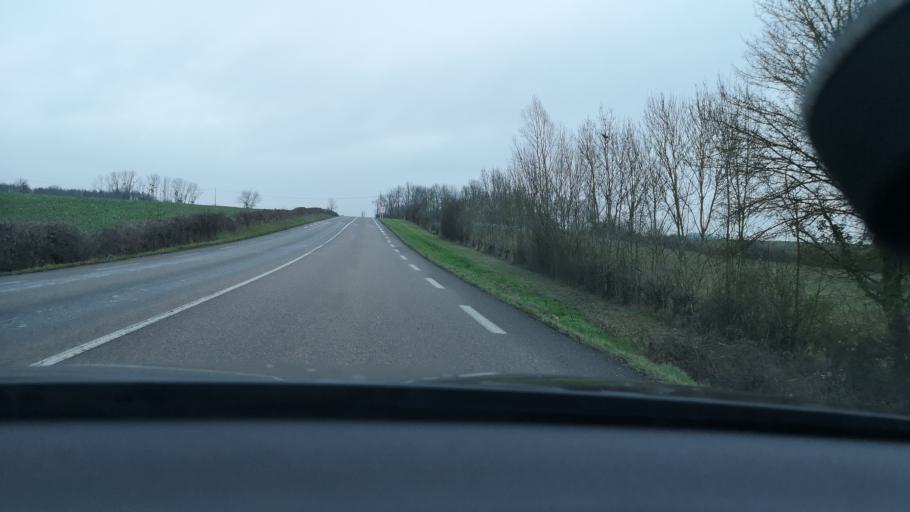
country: FR
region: Bourgogne
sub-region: Departement de la Cote-d'Or
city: Seurre
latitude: 46.9467
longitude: 5.1554
